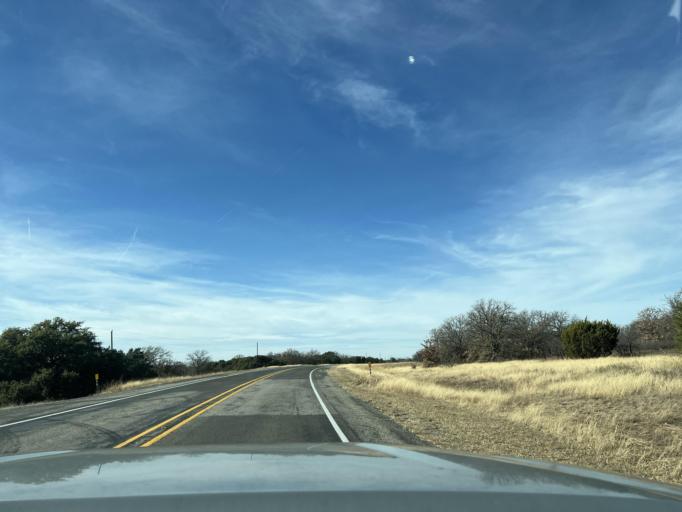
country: US
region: Texas
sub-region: Eastland County
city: Cisco
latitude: 32.4650
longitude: -99.0327
